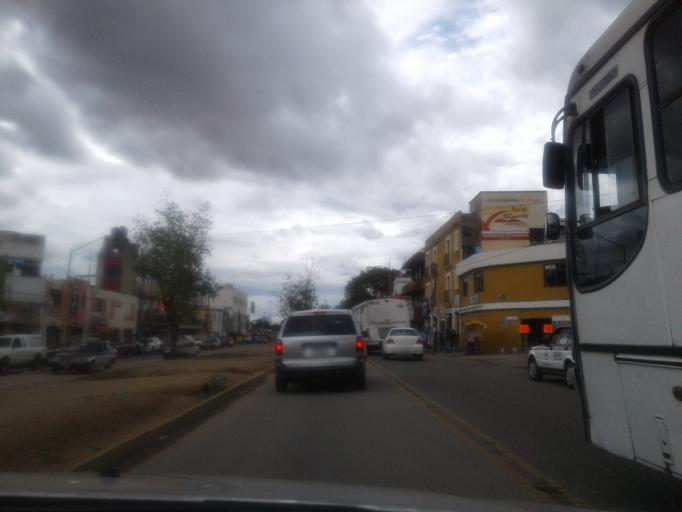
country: MX
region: Oaxaca
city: Oaxaca de Juarez
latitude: 17.0570
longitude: -96.7308
